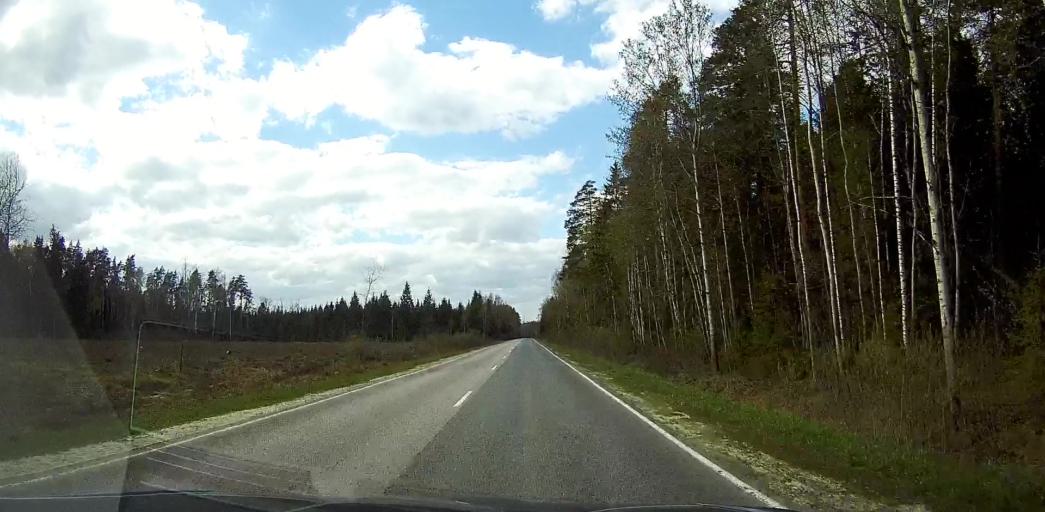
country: RU
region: Moskovskaya
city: Rakhmanovo
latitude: 55.6484
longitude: 38.6677
